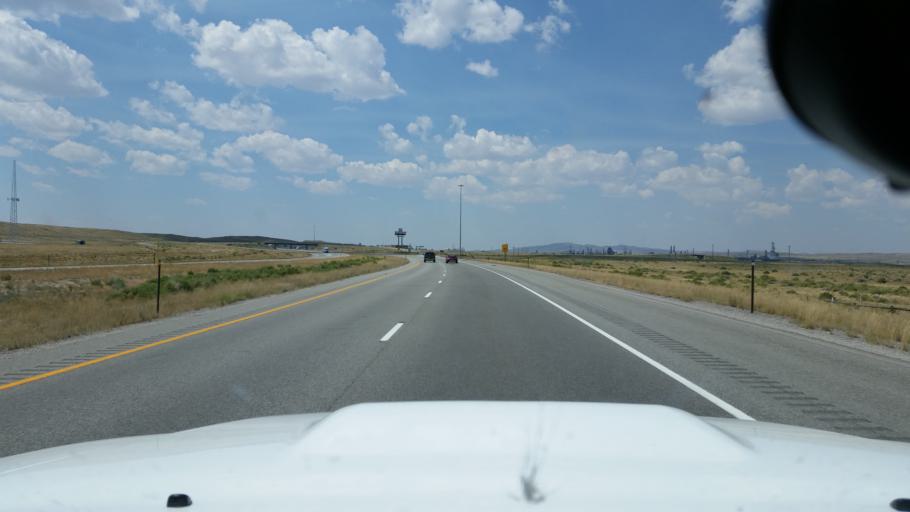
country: US
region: Wyoming
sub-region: Carbon County
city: Rawlins
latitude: 41.7736
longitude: -107.0717
